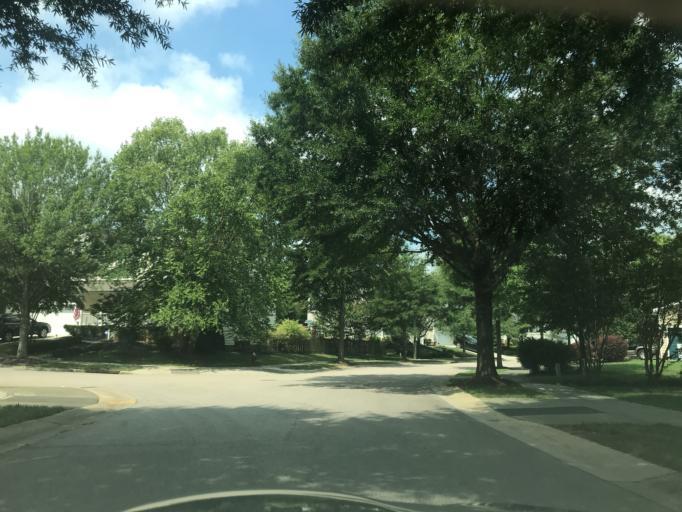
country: US
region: North Carolina
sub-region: Wake County
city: Wake Forest
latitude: 35.9278
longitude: -78.5613
